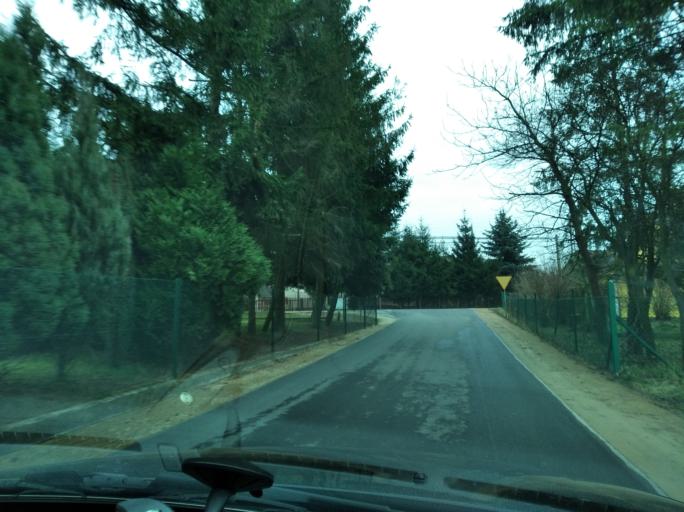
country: PL
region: Subcarpathian Voivodeship
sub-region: Powiat lancucki
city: Rakszawa
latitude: 50.1548
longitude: 22.2410
